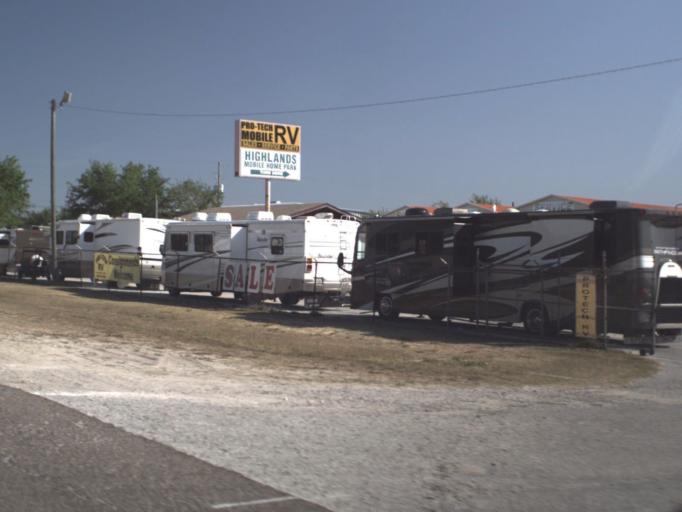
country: US
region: Florida
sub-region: Lake County
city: Minneola
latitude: 28.6040
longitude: -81.7556
